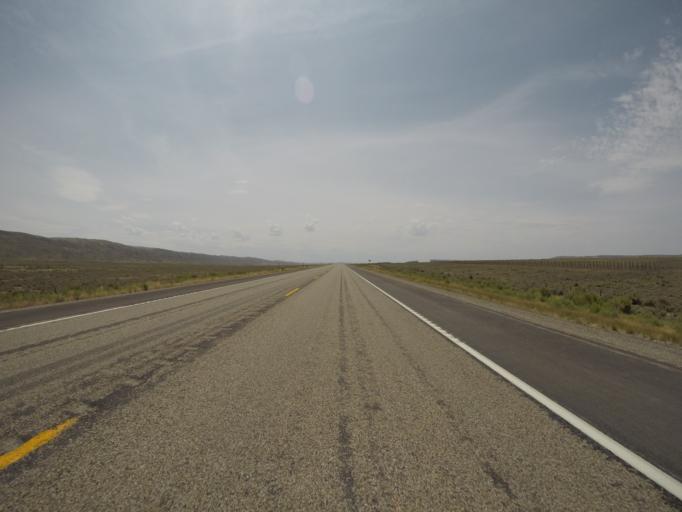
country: US
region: Wyoming
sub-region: Lincoln County
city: Kemmerer
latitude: 41.6820
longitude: -110.5680
